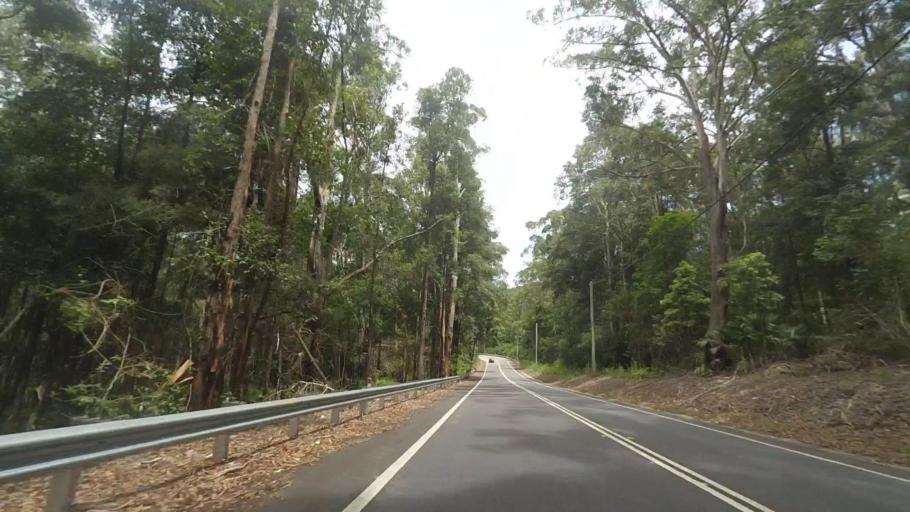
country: AU
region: New South Wales
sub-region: Wyong Shire
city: Chittaway Bay
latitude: -33.3365
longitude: 151.4131
